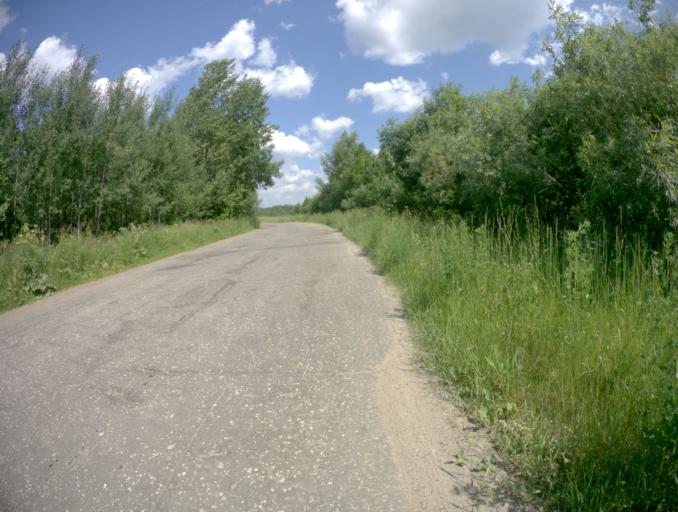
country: RU
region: Vladimir
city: Vyazniki
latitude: 56.3154
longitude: 42.1263
